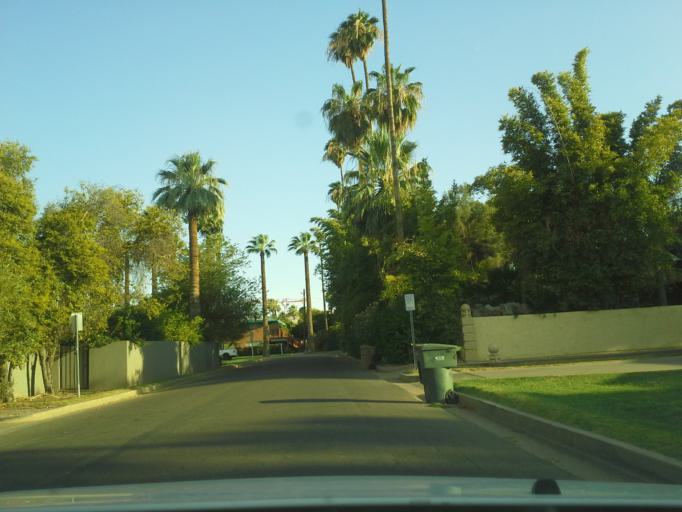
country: US
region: Arizona
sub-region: Maricopa County
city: Phoenix
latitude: 33.4702
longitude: -112.0712
